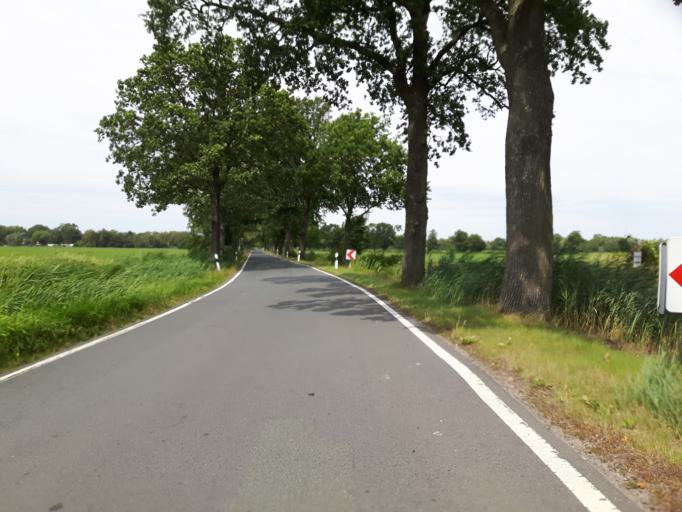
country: DE
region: Lower Saxony
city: Rastede
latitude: 53.3381
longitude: 8.2491
